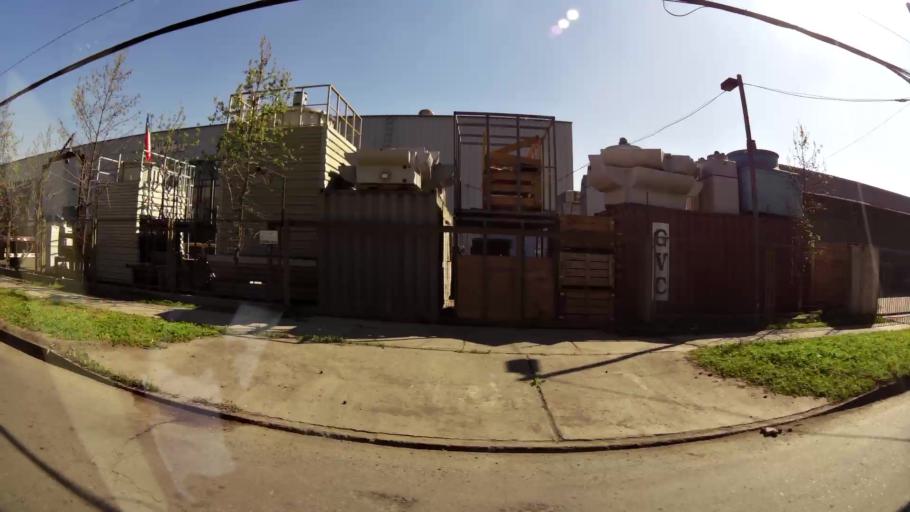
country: CL
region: Santiago Metropolitan
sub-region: Provincia de Chacabuco
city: Chicureo Abajo
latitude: -33.3288
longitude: -70.7074
